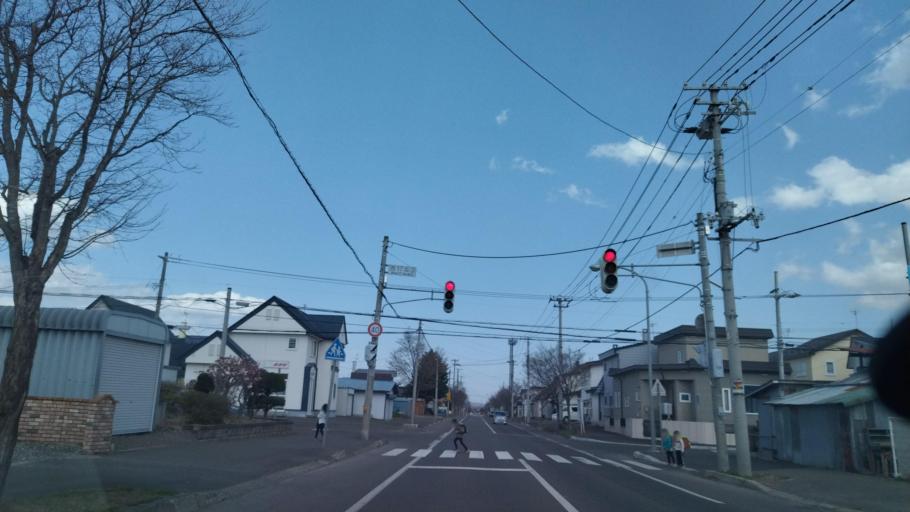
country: JP
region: Hokkaido
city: Obihiro
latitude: 42.9393
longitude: 143.1648
